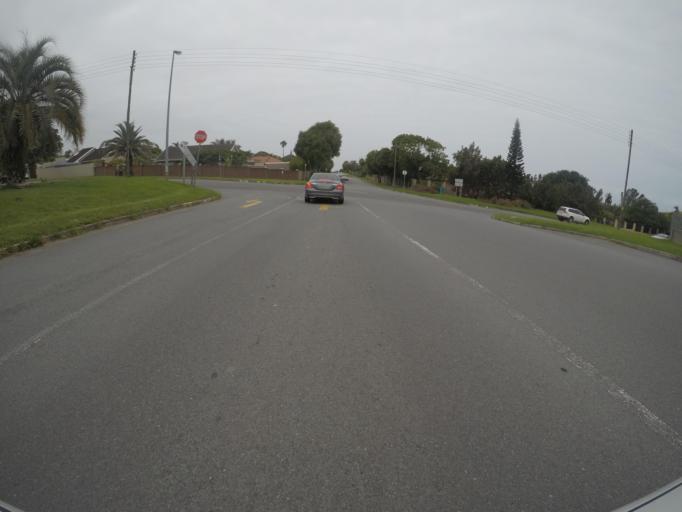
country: ZA
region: Eastern Cape
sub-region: Buffalo City Metropolitan Municipality
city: East London
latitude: -32.9691
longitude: 27.9412
